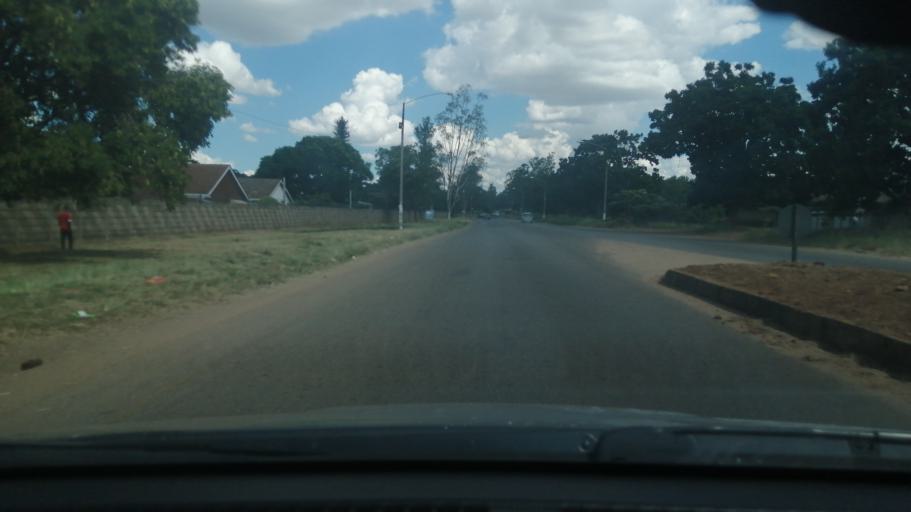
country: ZW
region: Harare
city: Harare
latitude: -17.8499
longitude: 31.0818
